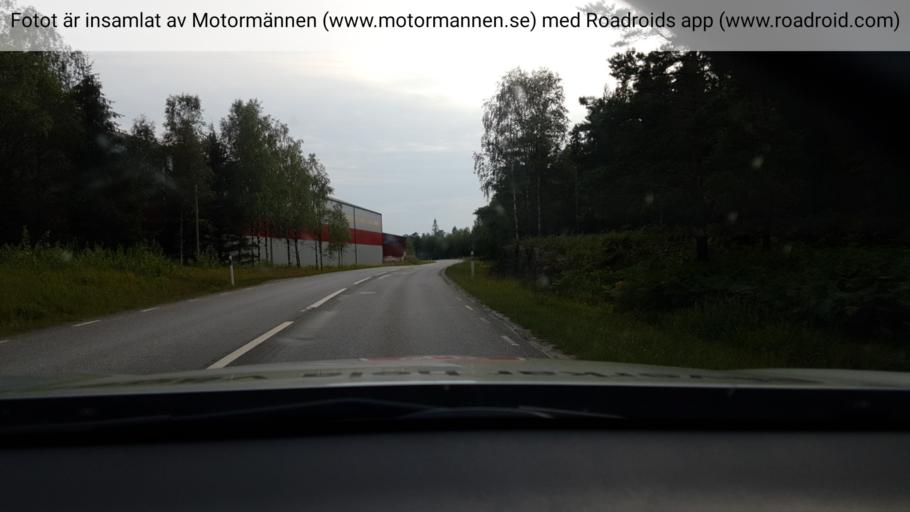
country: SE
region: Vaestra Goetaland
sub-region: Uddevalla Kommun
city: Uddevalla
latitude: 58.3756
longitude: 11.9815
